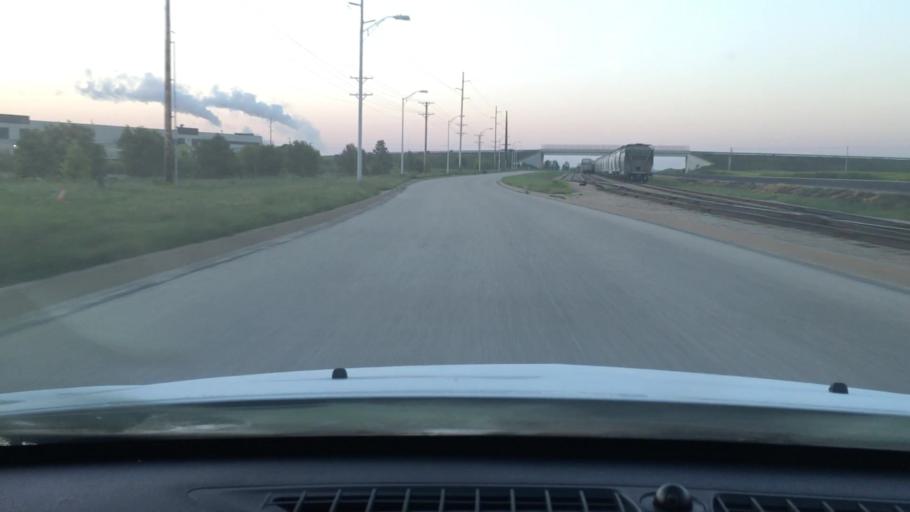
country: US
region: Illinois
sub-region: Ogle County
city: Rochelle
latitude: 41.9016
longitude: -89.0439
